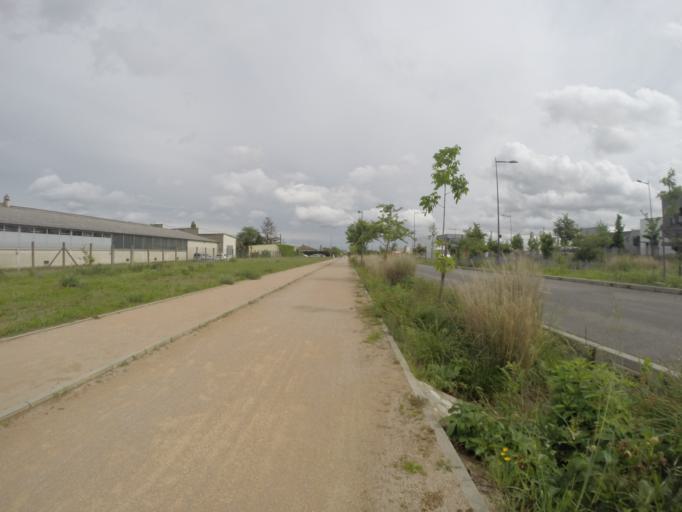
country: FR
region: Rhone-Alpes
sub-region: Departement du Rhone
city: Bron
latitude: 45.7524
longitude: 4.9320
